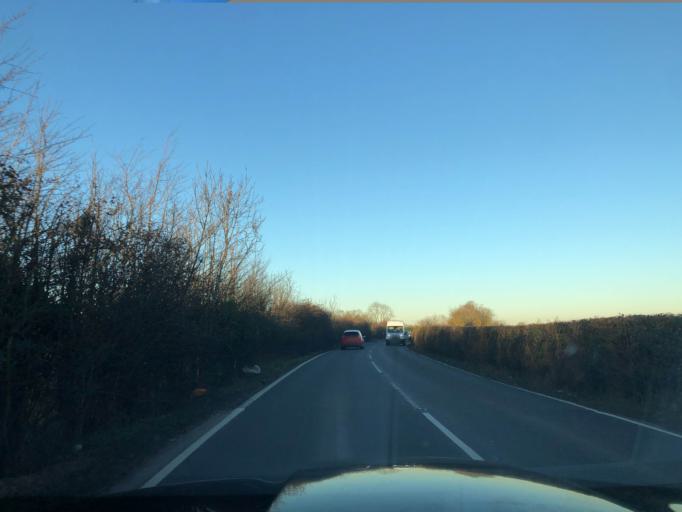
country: GB
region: England
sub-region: Warwickshire
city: Harbury
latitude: 52.1957
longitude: -1.4547
